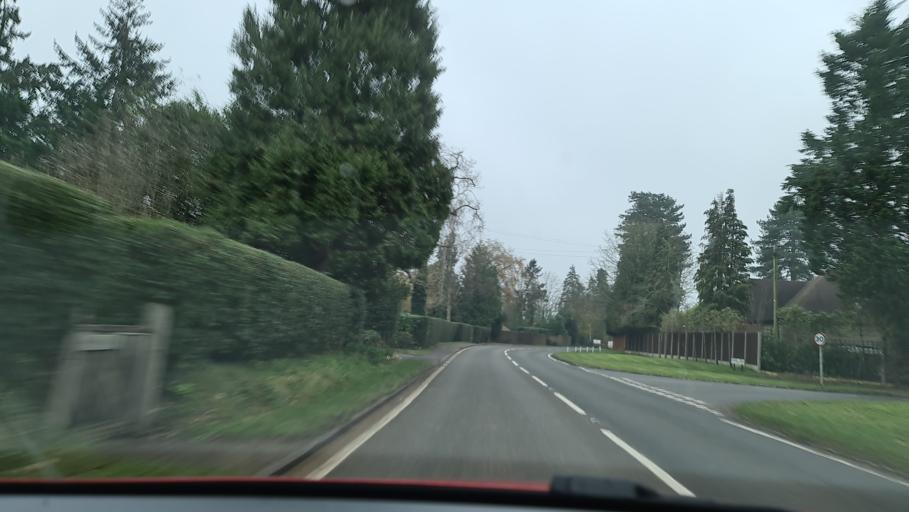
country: GB
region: England
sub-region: Buckinghamshire
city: Beaconsfield
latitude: 51.6275
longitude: -0.6556
